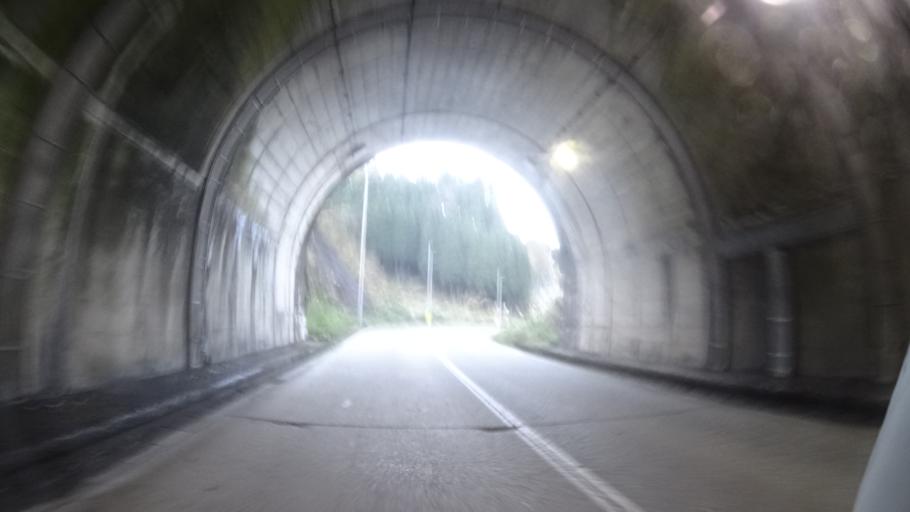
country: JP
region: Fukui
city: Ono
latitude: 35.9608
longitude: 136.6065
